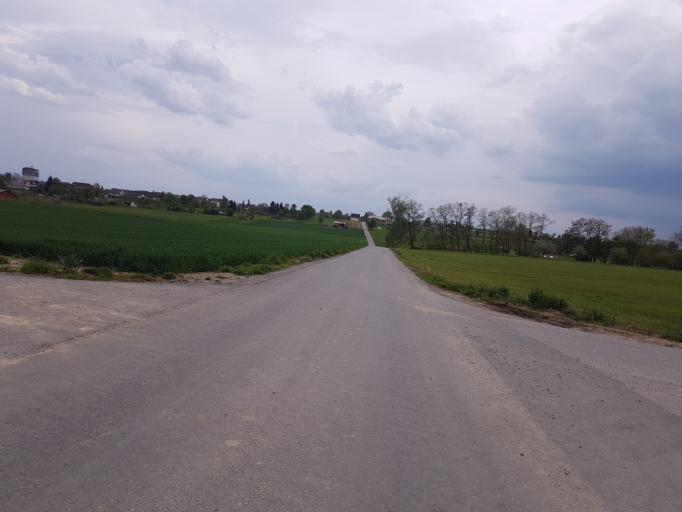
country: DE
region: Baden-Wuerttemberg
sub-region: Regierungsbezirk Stuttgart
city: Bondorf
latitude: 48.5285
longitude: 8.8220
